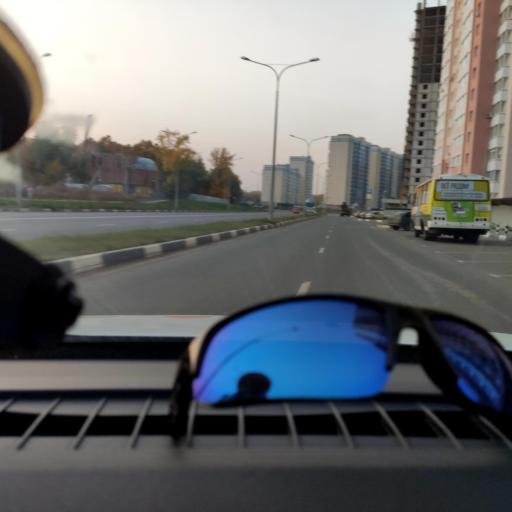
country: RU
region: Samara
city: Samara
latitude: 53.1464
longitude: 50.0758
